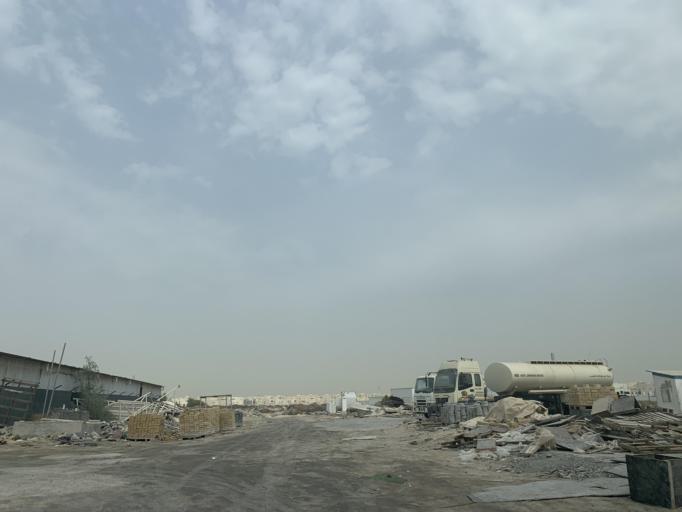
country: BH
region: Northern
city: Madinat `Isa
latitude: 26.1744
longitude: 50.5072
